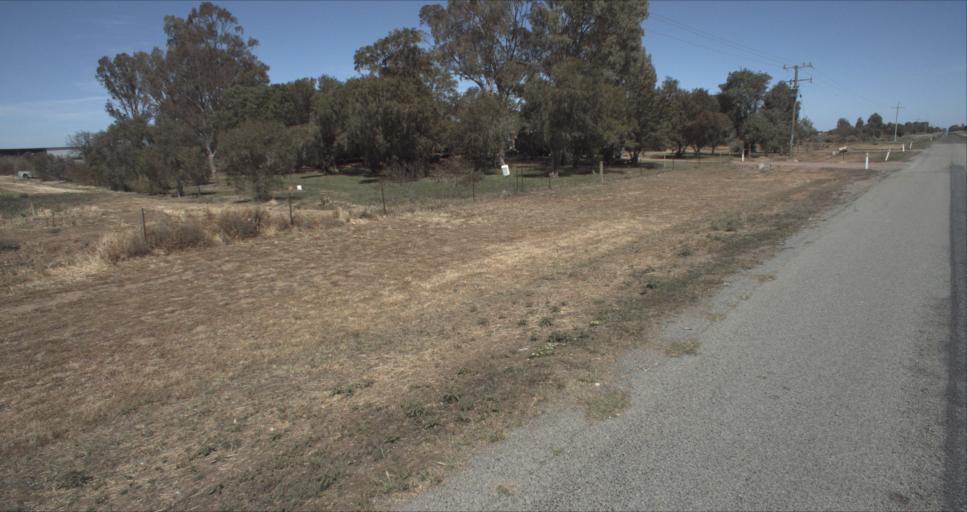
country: AU
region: New South Wales
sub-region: Leeton
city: Leeton
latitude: -34.5825
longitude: 146.3015
